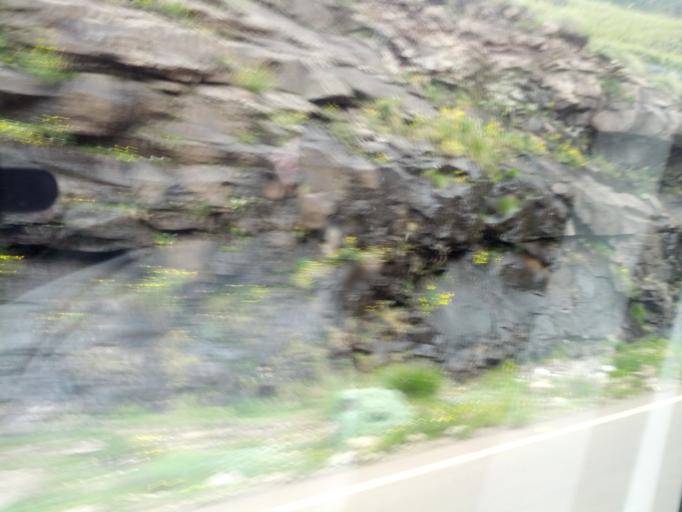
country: LS
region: Butha-Buthe
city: Butha-Buthe
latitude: -29.0717
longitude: 28.3816
